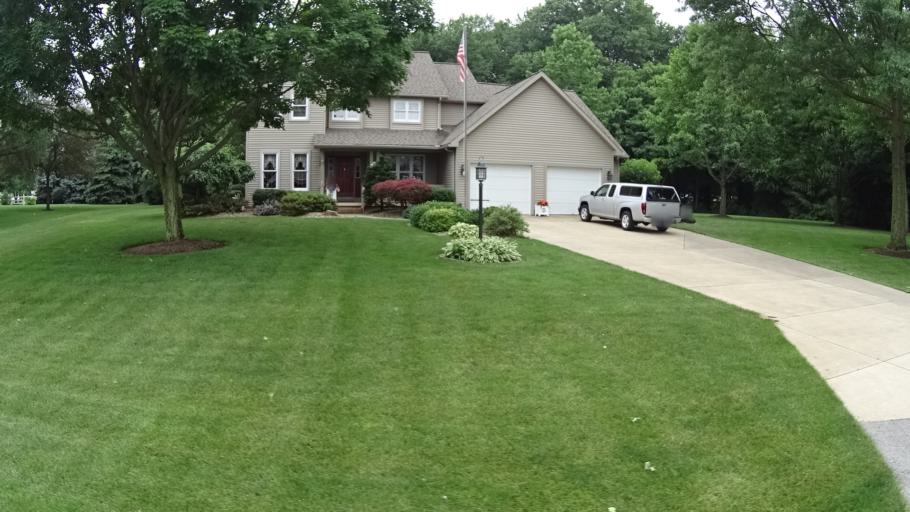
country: US
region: Ohio
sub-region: Erie County
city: Milan
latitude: 41.3003
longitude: -82.5835
